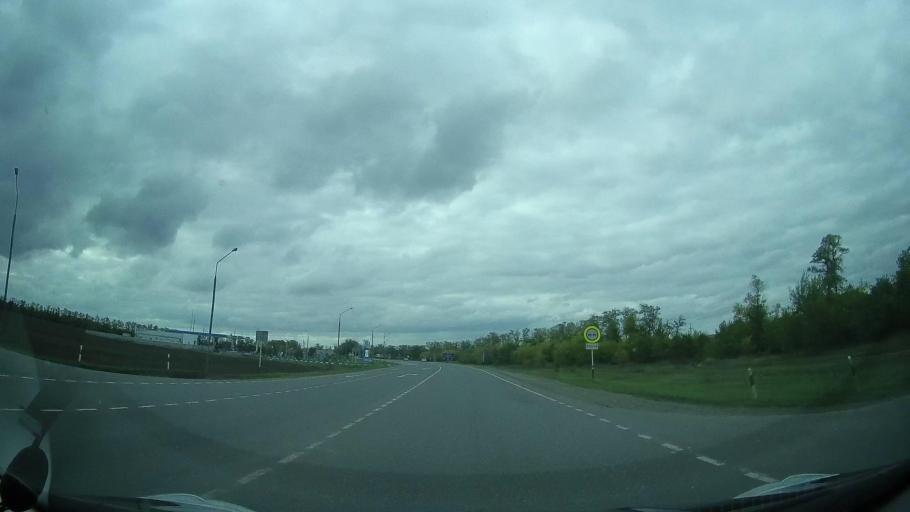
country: RU
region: Rostov
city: Mechetinskaya
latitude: 46.7549
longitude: 40.4571
